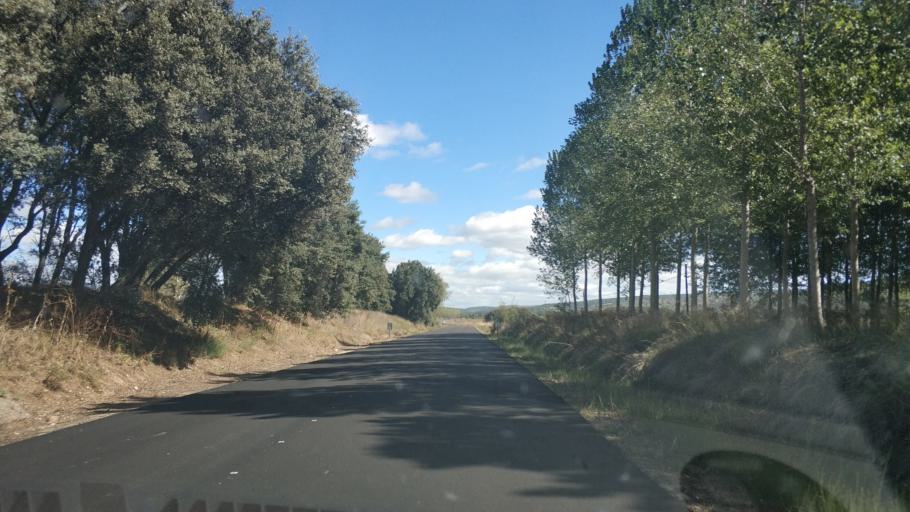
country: ES
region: Castille and Leon
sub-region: Provincia de Burgos
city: Puentedura
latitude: 42.0337
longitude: -3.6141
